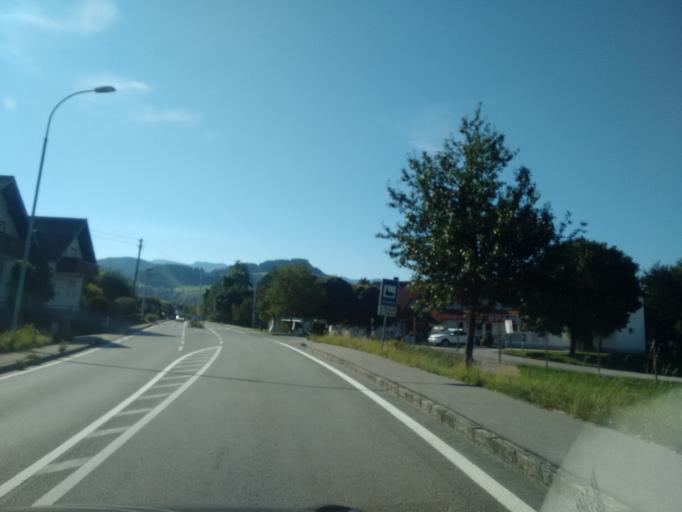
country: AT
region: Upper Austria
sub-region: Politischer Bezirk Vocklabruck
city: Attersee
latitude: 47.9079
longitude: 13.5723
